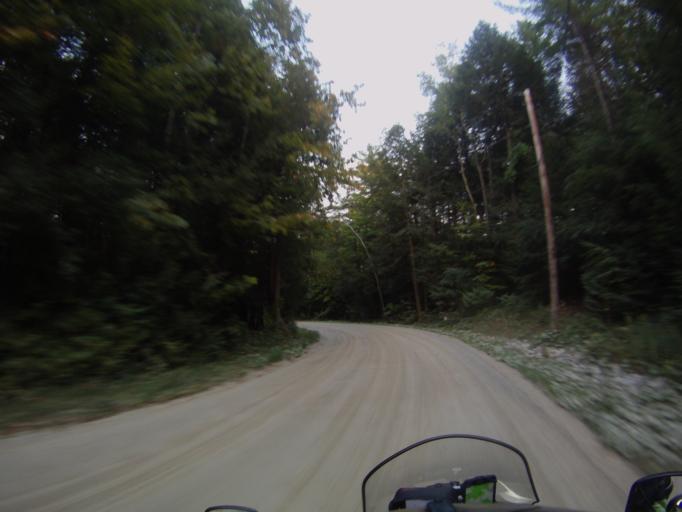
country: US
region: Vermont
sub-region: Rutland County
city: Brandon
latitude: 43.7819
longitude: -73.1336
